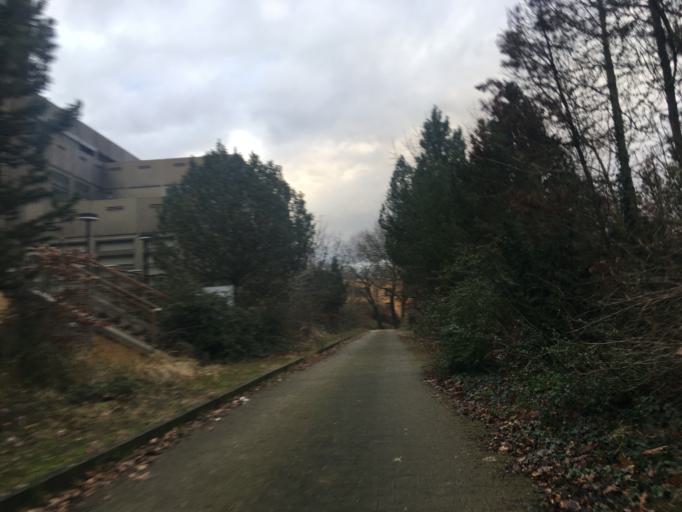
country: DE
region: Berlin
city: Wittenau
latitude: 52.5803
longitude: 13.3232
